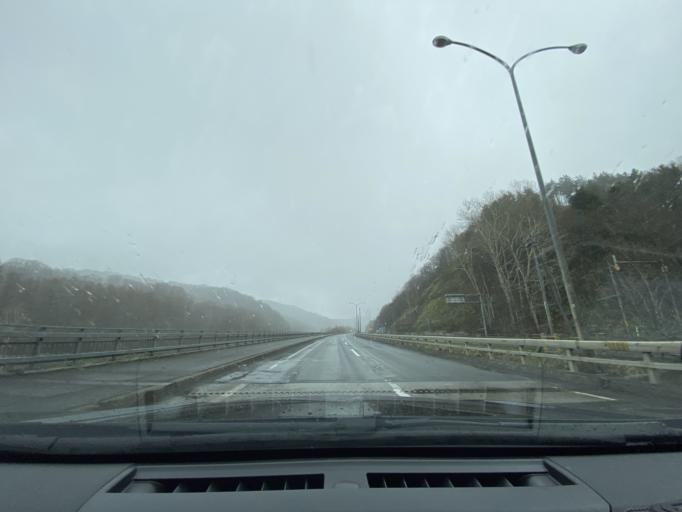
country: JP
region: Hokkaido
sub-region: Asahikawa-shi
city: Asahikawa
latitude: 43.7278
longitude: 142.2203
